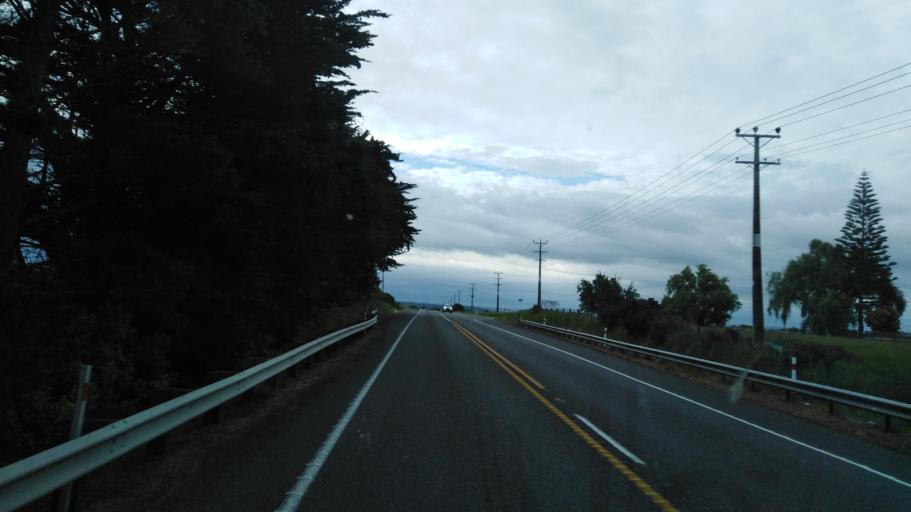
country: NZ
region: Manawatu-Wanganui
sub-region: Rangitikei District
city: Bulls
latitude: -40.1406
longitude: 175.3669
